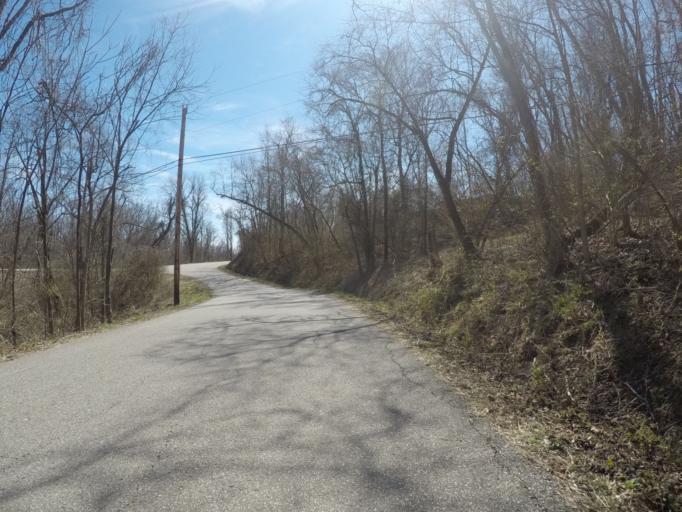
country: US
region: West Virginia
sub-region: Cabell County
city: Huntington
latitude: 38.4555
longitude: -82.4930
